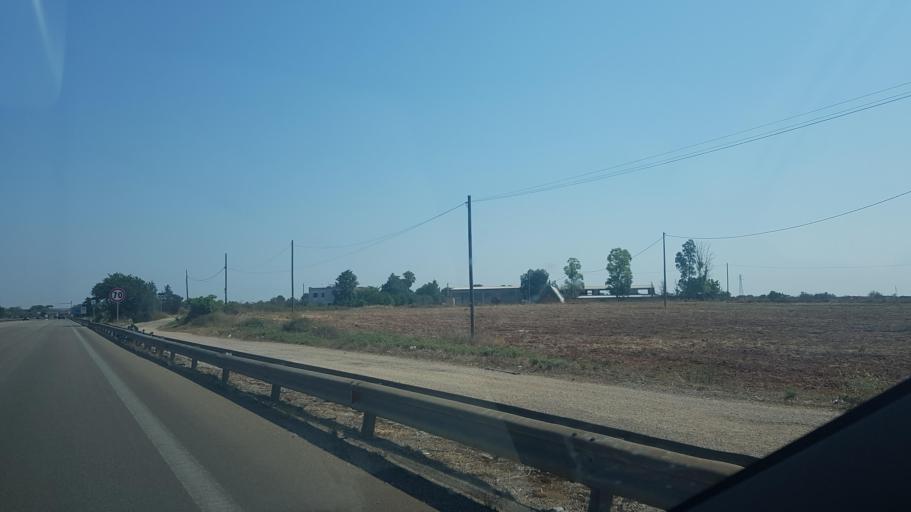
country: IT
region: Apulia
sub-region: Provincia di Lecce
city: Scorrano
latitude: 40.0884
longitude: 18.3100
